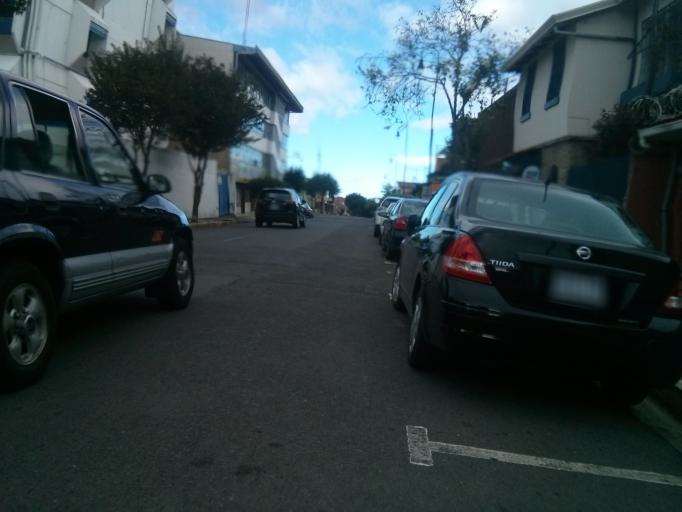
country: CR
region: San Jose
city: Calle Blancos
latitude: 9.9379
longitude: -84.0675
